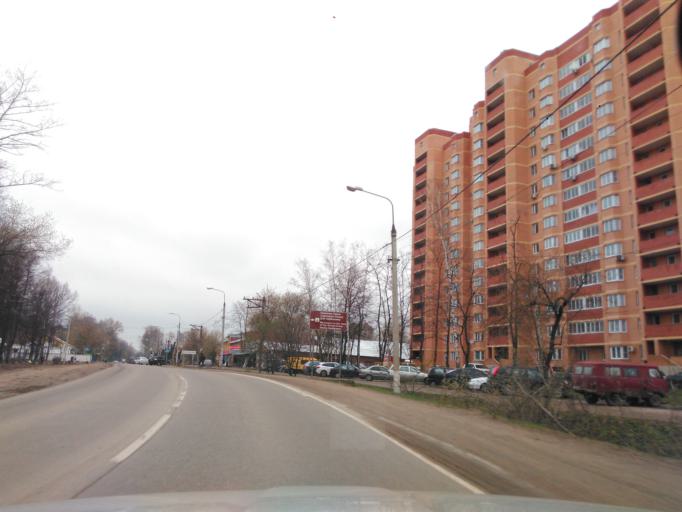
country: RU
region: Moskovskaya
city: Nakhabino
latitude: 55.8390
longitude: 37.1625
